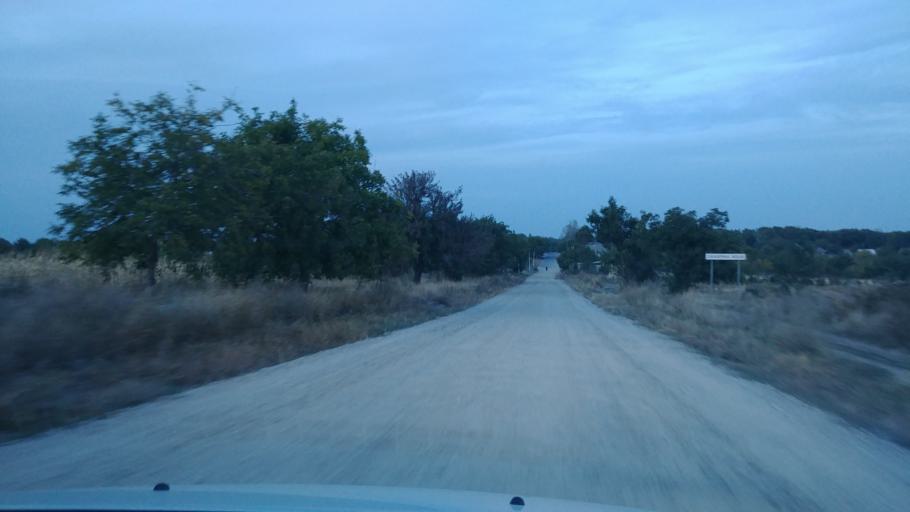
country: MD
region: Rezina
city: Saharna
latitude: 47.6711
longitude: 28.9501
